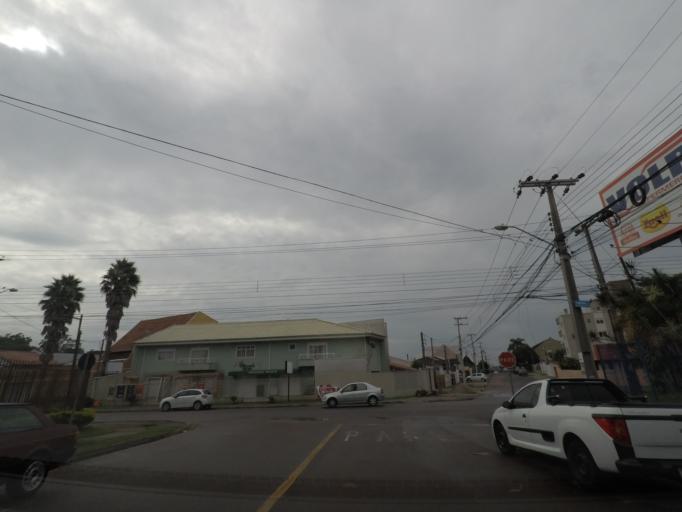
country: BR
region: Parana
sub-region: Curitiba
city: Curitiba
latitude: -25.4727
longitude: -49.3118
